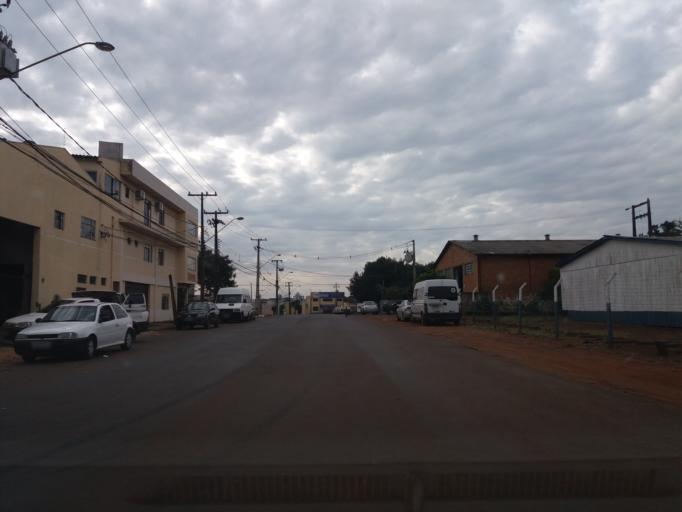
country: BR
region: Parana
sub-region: Cascavel
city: Cascavel
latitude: -24.9828
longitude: -53.4644
